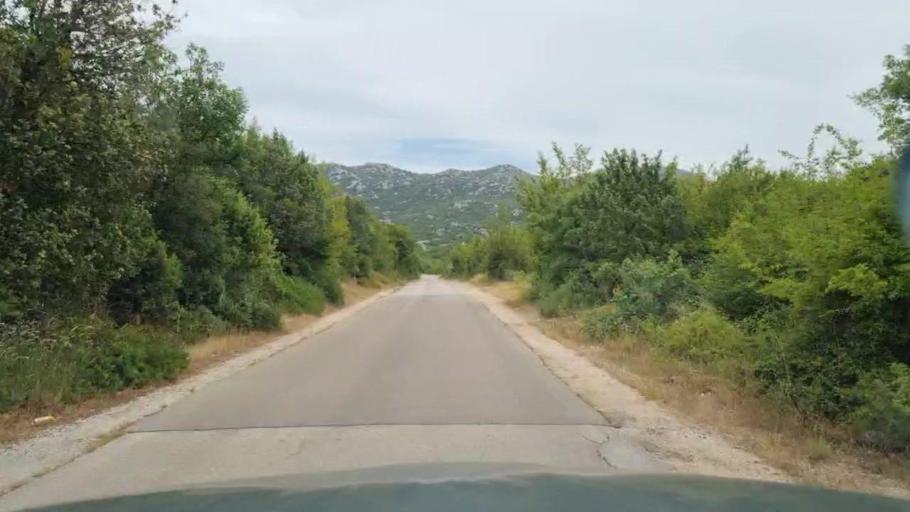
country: BA
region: Federation of Bosnia and Herzegovina
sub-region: Hercegovacko-Bosanski Kanton
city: Neum
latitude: 42.9256
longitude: 17.6744
